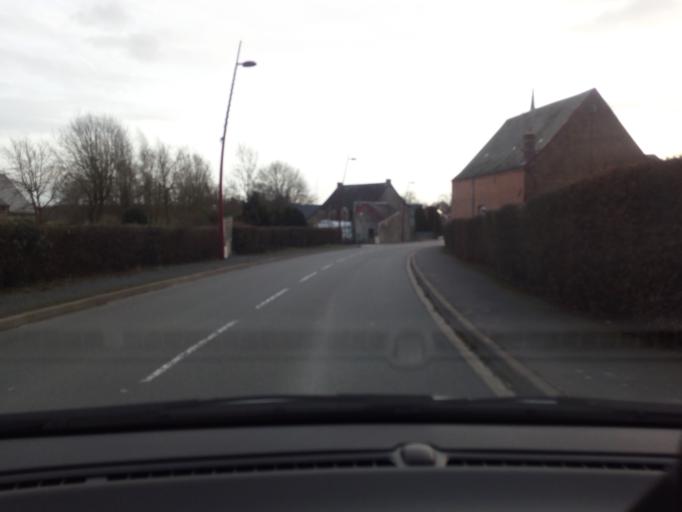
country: FR
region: Nord-Pas-de-Calais
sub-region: Departement du Nord
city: La Longueville
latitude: 50.3247
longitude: 3.8676
